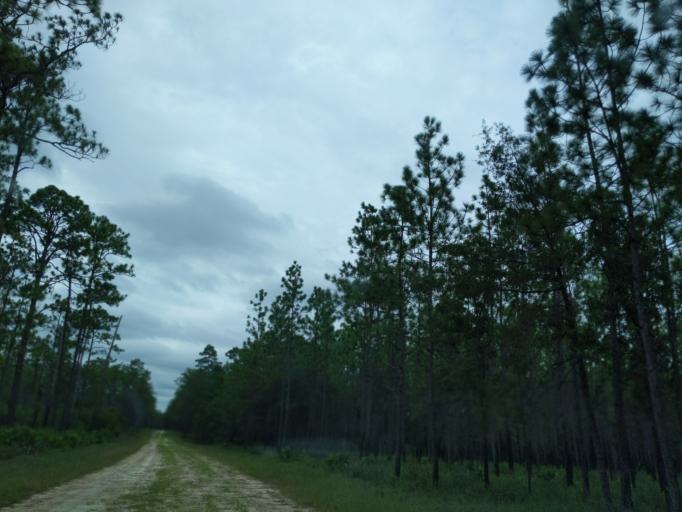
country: US
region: Florida
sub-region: Gadsden County
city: Midway
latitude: 30.3883
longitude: -84.4653
